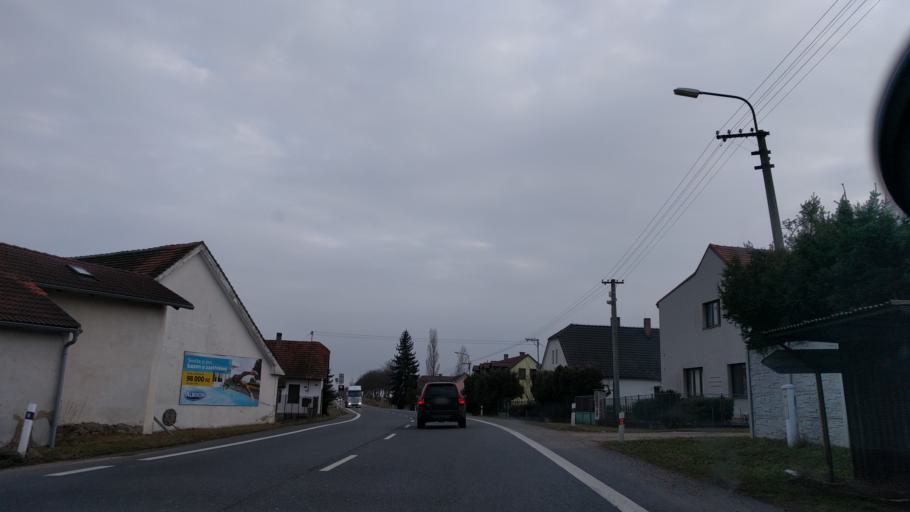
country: CZ
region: Jihocesky
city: Cimelice
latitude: 49.4854
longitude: 14.0707
